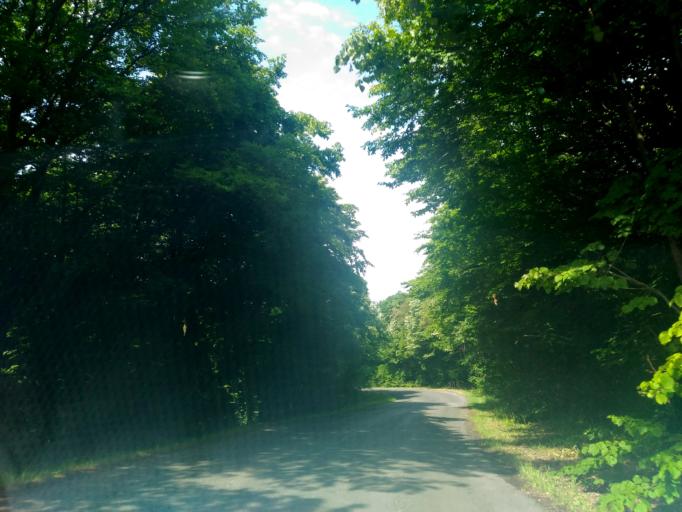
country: HU
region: Baranya
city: Pecs
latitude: 46.1190
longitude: 18.2088
